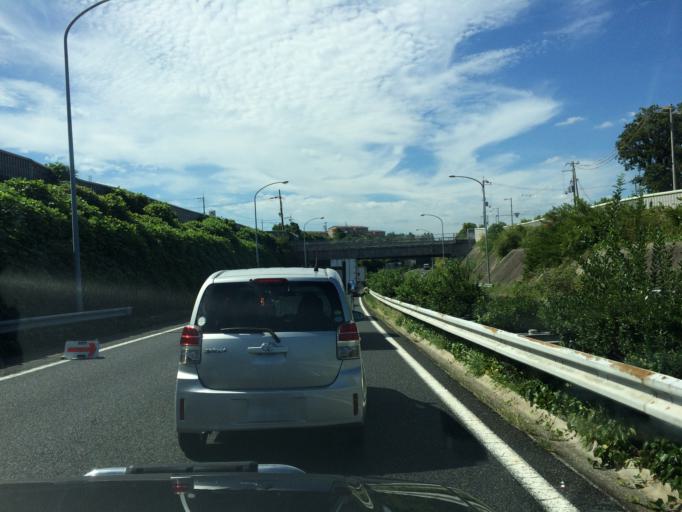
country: JP
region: Osaka
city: Takaishi
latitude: 34.5012
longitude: 135.4871
